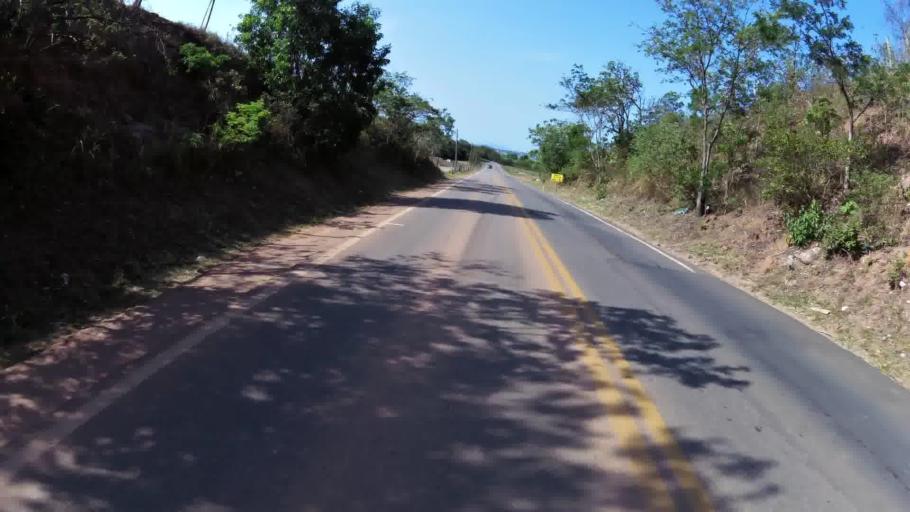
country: BR
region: Espirito Santo
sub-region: Piuma
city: Piuma
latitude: -20.8801
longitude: -40.7656
